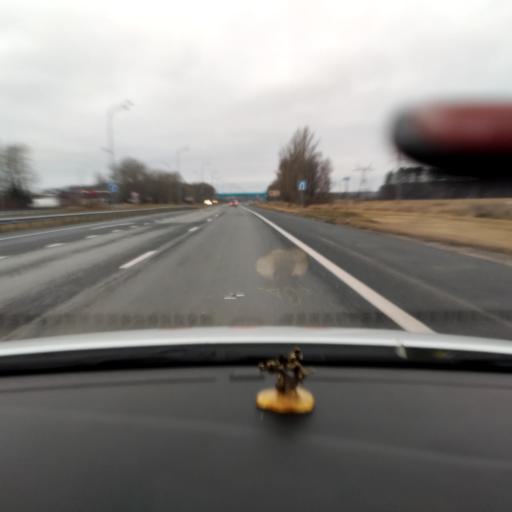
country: RU
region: Tatarstan
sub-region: Zelenodol'skiy Rayon
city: Vasil'yevo
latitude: 55.8721
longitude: 48.6781
